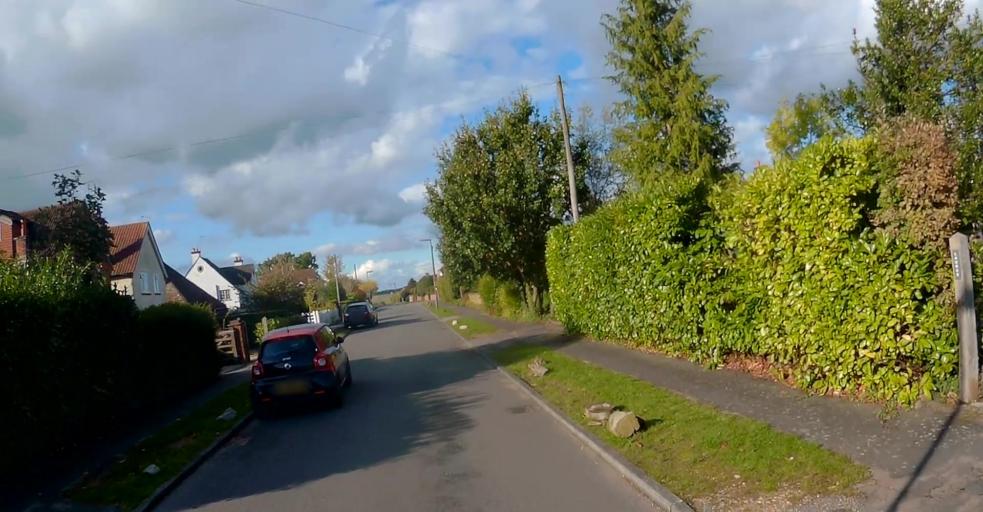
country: GB
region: England
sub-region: Surrey
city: Farnham
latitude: 51.1966
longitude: -0.8104
